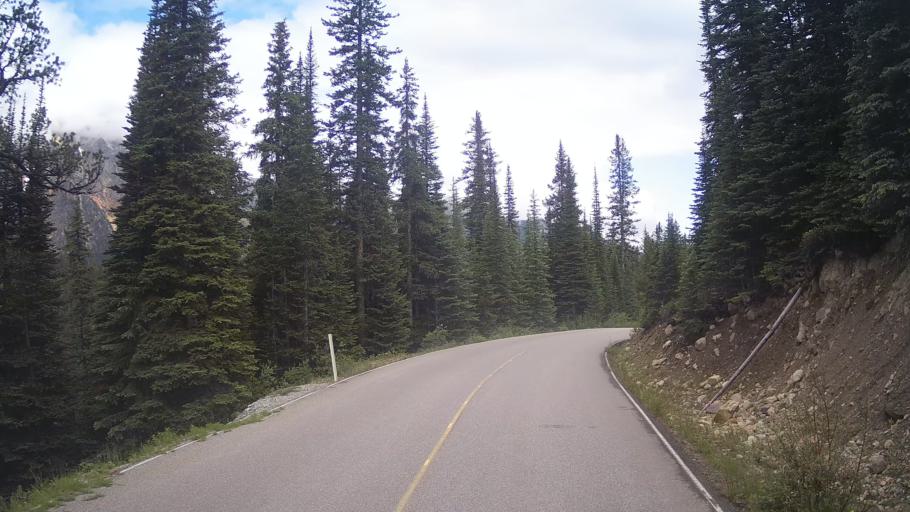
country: CA
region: Alberta
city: Jasper Park Lodge
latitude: 52.6966
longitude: -118.0583
